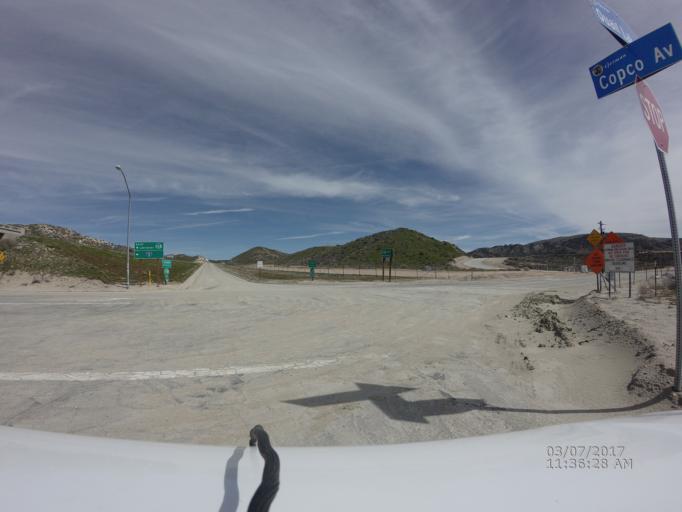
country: US
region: California
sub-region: Kern County
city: Lebec
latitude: 34.7610
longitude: -118.7928
